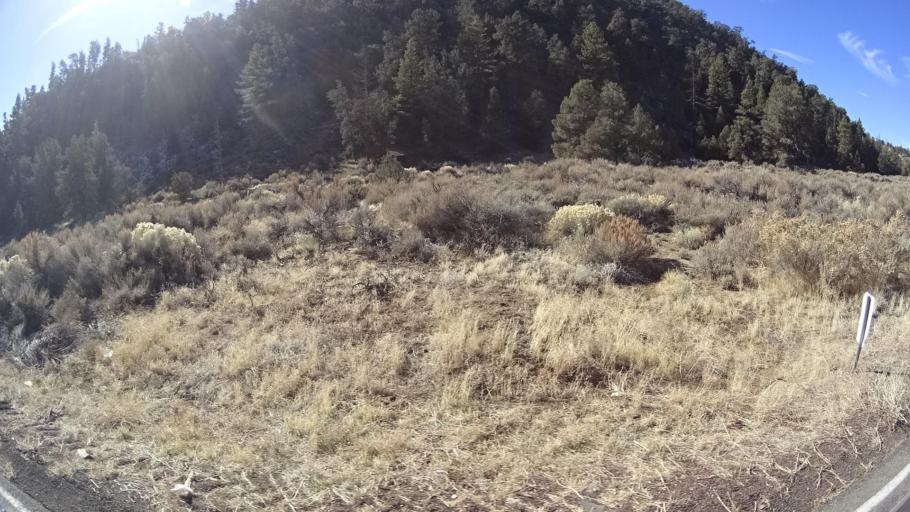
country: US
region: California
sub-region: Kern County
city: Frazier Park
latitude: 34.8208
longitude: -119.0056
